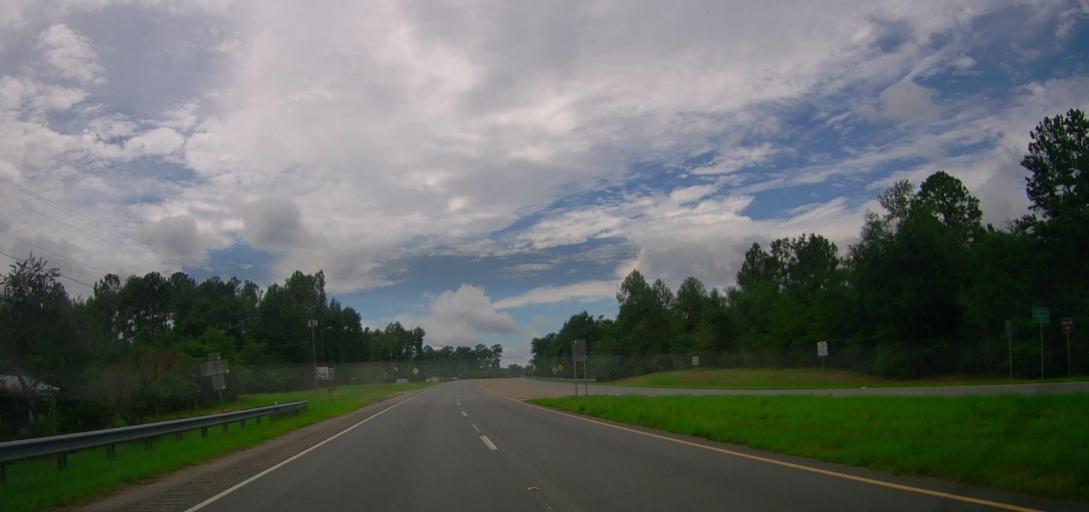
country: US
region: Georgia
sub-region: Telfair County
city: Helena
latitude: 32.1018
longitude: -83.0535
